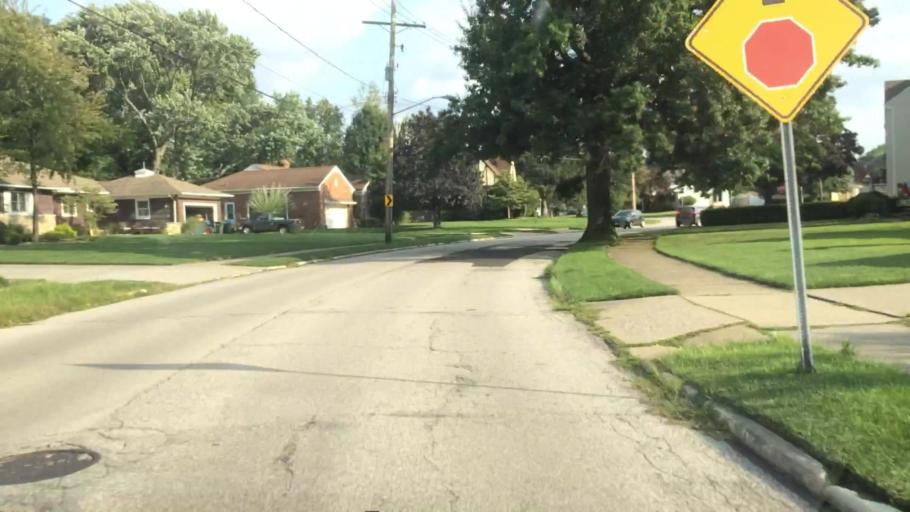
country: US
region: Ohio
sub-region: Cuyahoga County
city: Parma Heights
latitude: 41.4024
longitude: -81.7448
